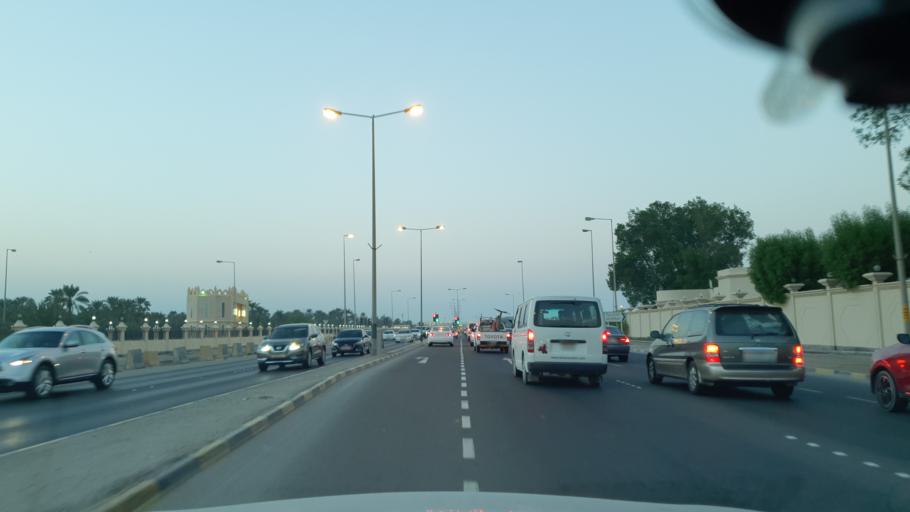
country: BH
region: Central Governorate
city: Madinat Hamad
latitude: 26.1811
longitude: 50.4658
